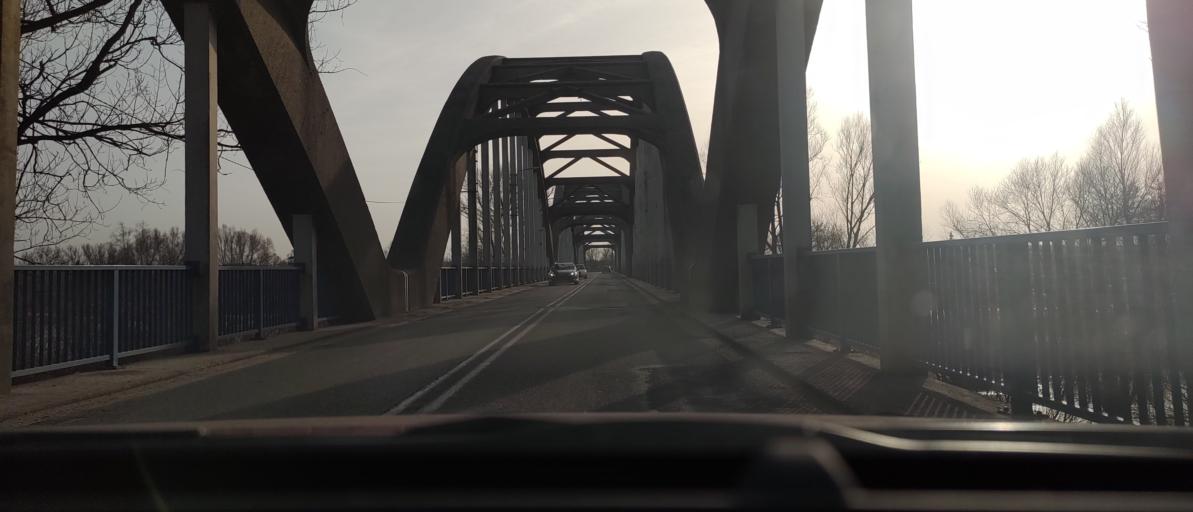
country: PL
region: Masovian Voivodeship
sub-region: Powiat bialobrzeski
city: Bialobrzegi
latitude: 51.6589
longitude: 20.9520
